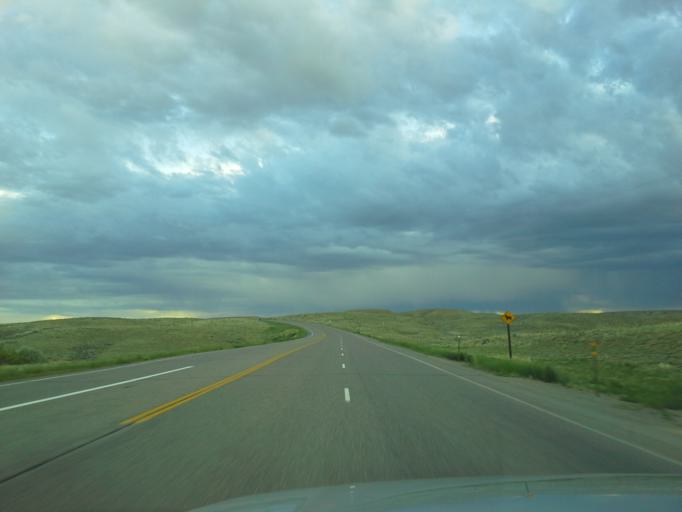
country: US
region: Wyoming
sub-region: Big Horn County
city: Basin
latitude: 44.3492
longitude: -108.0454
